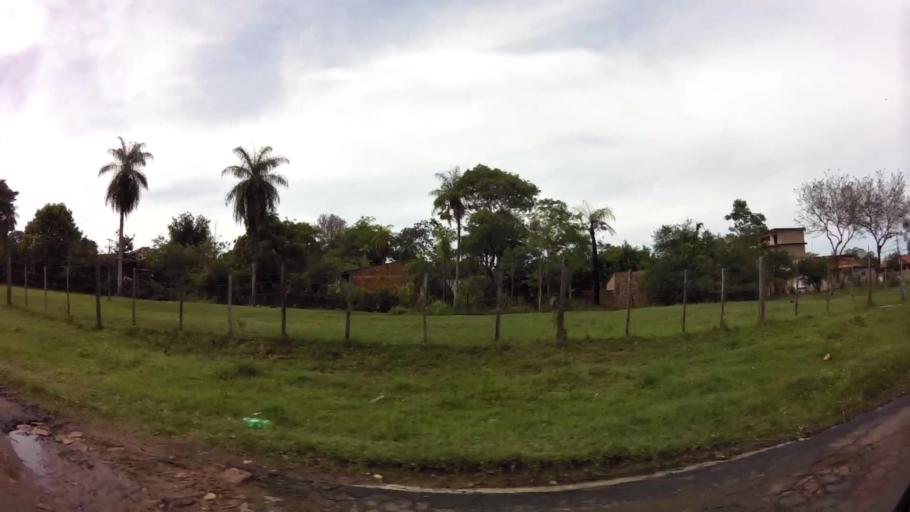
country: PY
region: Central
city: Limpio
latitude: -25.1641
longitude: -57.4782
